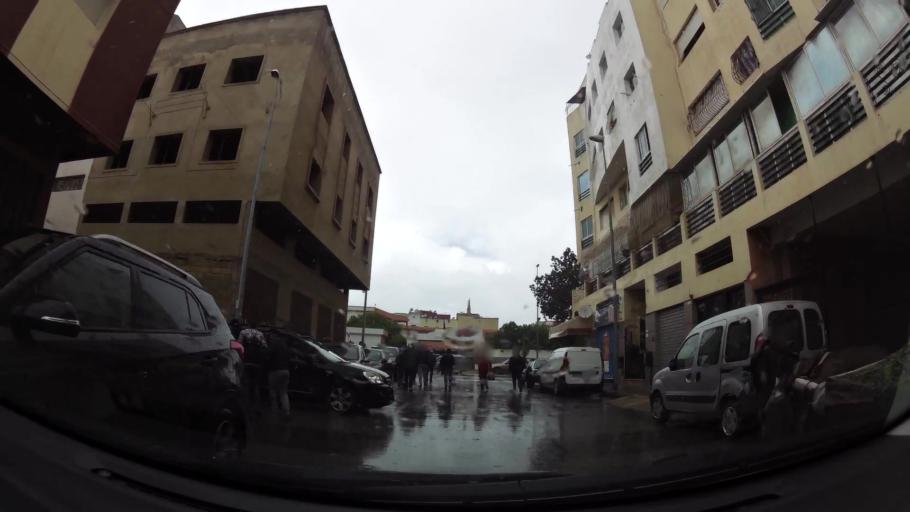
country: MA
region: Grand Casablanca
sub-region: Casablanca
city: Casablanca
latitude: 33.5487
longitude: -7.6791
